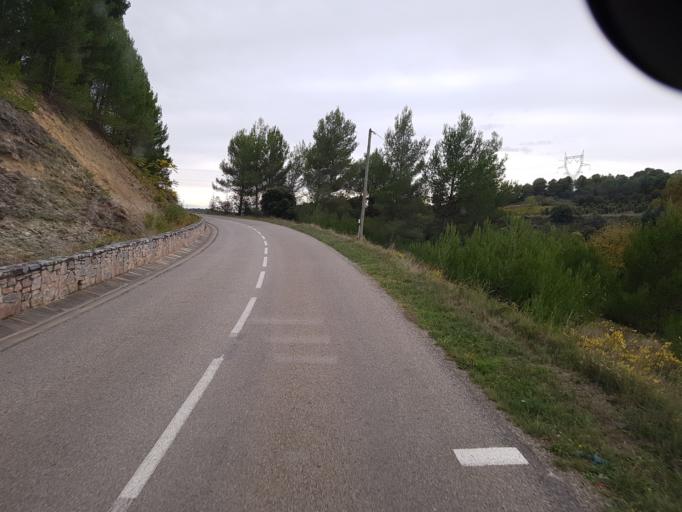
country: FR
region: Languedoc-Roussillon
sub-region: Departement de l'Aude
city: Conques-sur-Orbiel
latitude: 43.3081
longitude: 2.4636
